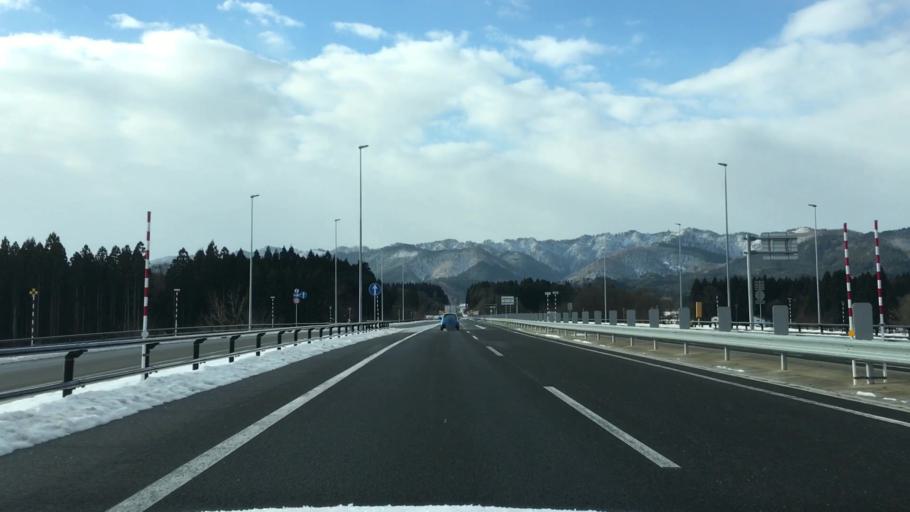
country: JP
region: Akita
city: Odate
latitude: 40.2492
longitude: 140.5150
